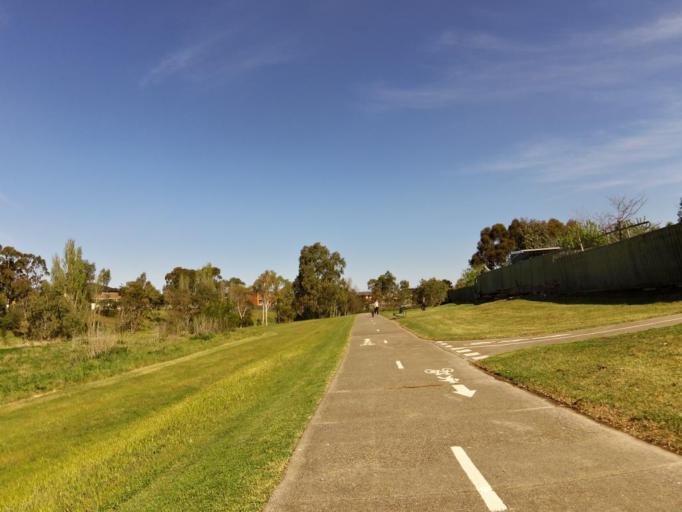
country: AU
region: Victoria
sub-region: Brimbank
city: Sunshine West
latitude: -37.7921
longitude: 144.8254
